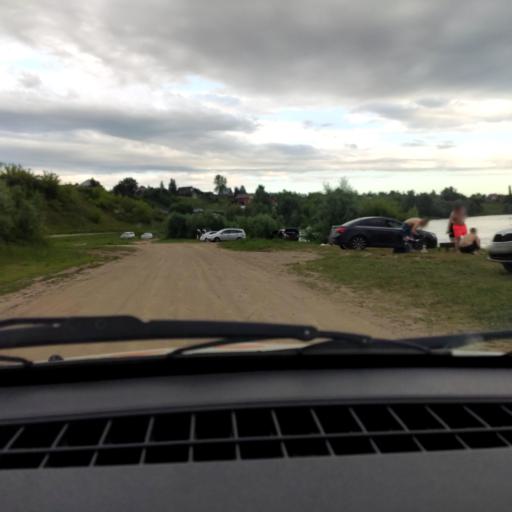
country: RU
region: Bashkortostan
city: Iglino
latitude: 54.7961
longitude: 56.2313
